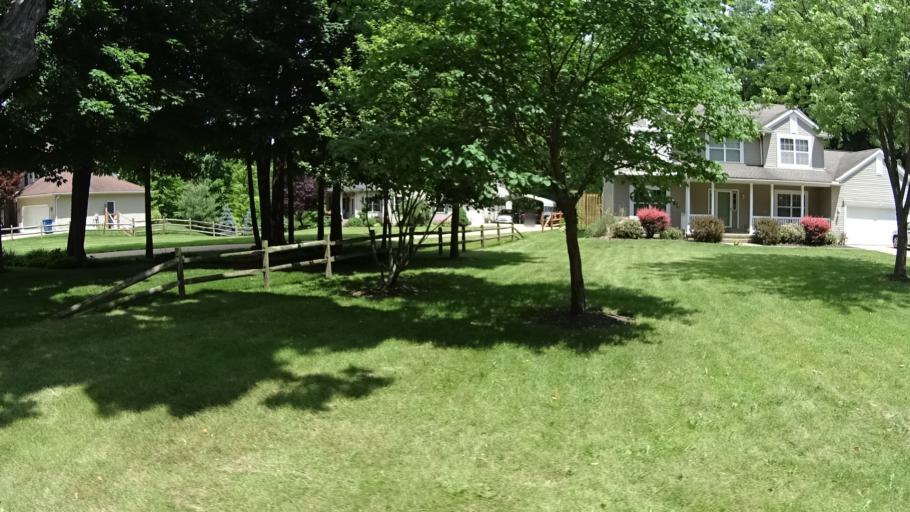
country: US
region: Ohio
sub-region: Erie County
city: Milan
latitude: 41.3029
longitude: -82.5991
